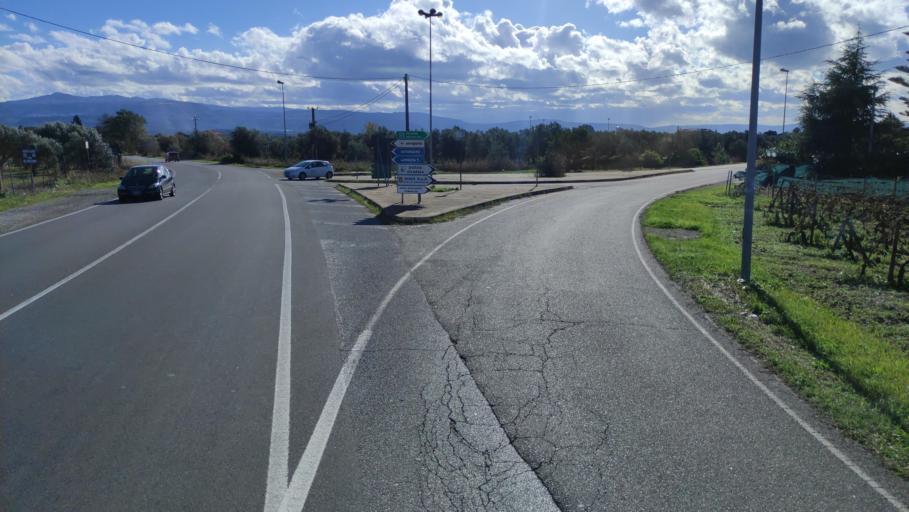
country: IT
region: Calabria
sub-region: Provincia di Catanzaro
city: Santa Eufemia Lamezia
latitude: 38.9287
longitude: 16.2858
